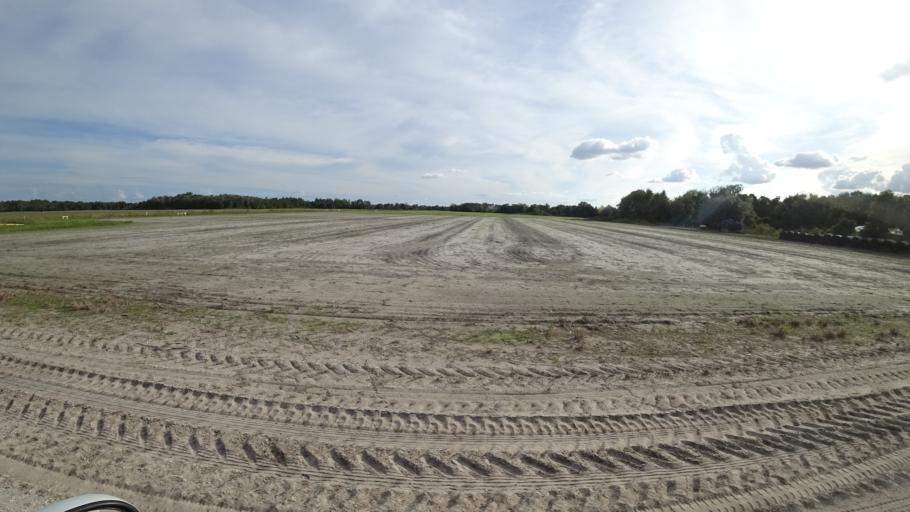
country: US
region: Florida
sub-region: Hillsborough County
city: Wimauma
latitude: 27.5665
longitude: -82.0827
